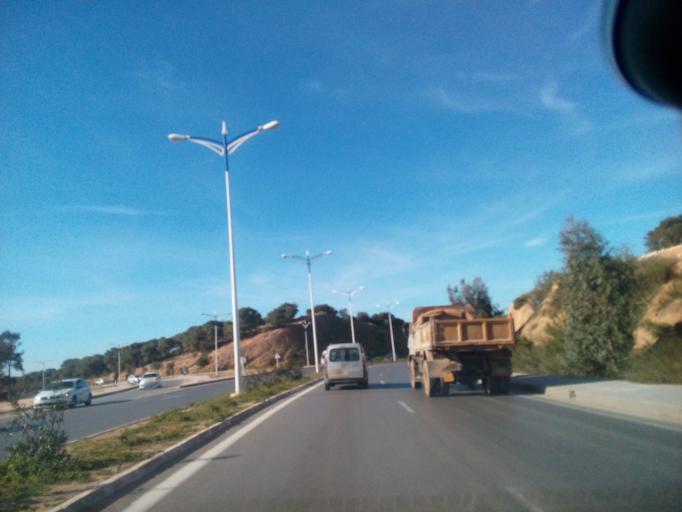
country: DZ
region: Mostaganem
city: Mostaganem
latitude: 35.9425
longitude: 0.1001
